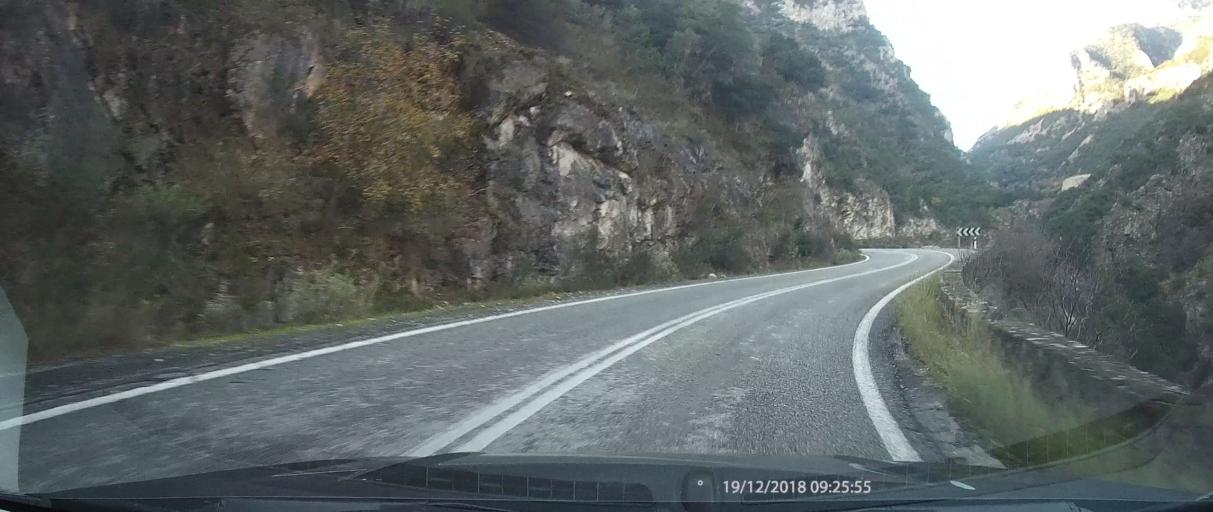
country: GR
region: Peloponnese
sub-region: Nomos Lakonias
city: Magoula
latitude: 37.0939
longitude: 22.3331
